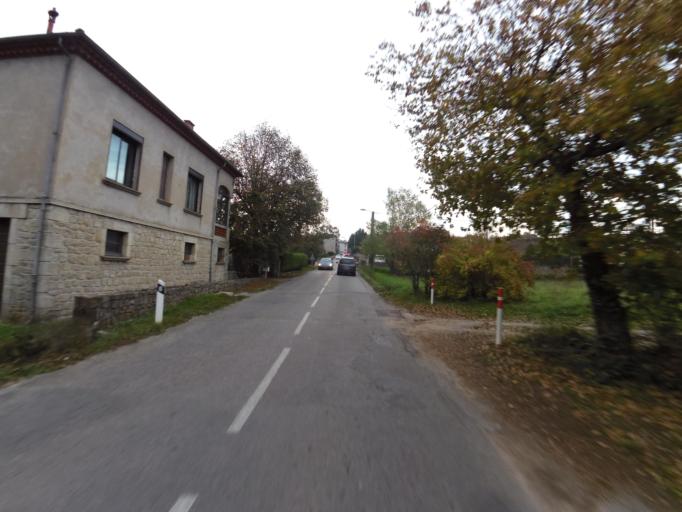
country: FR
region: Rhone-Alpes
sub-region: Departement de l'Ardeche
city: Lablachere
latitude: 44.4640
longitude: 4.2112
